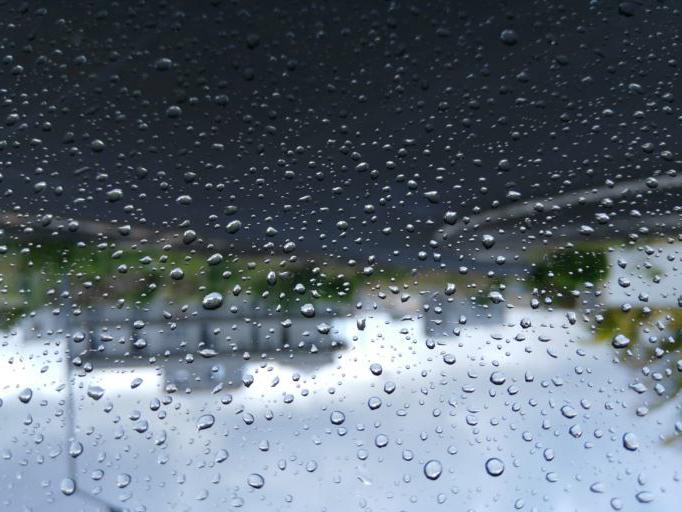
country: MU
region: Plaines Wilhems
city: Ebene
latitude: -20.2440
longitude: 57.4821
